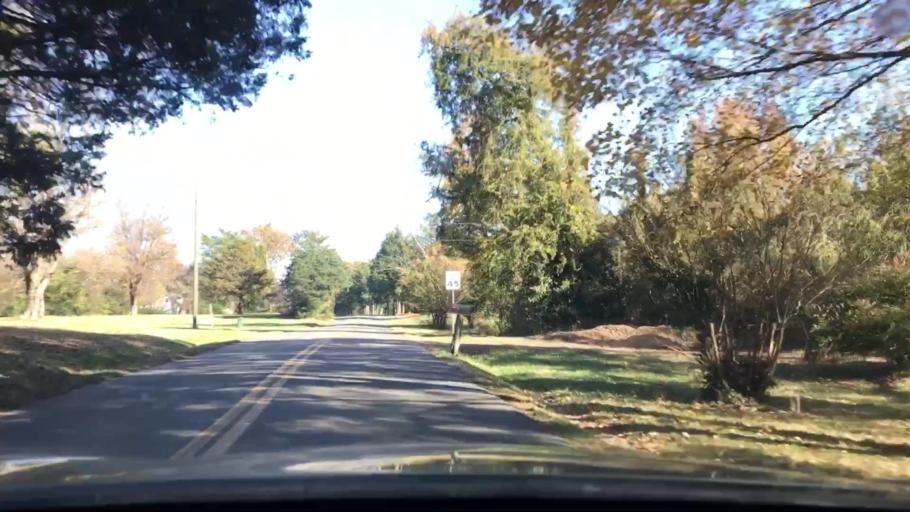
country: US
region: Virginia
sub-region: Henrico County
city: Short Pump
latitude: 37.6667
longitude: -77.7081
